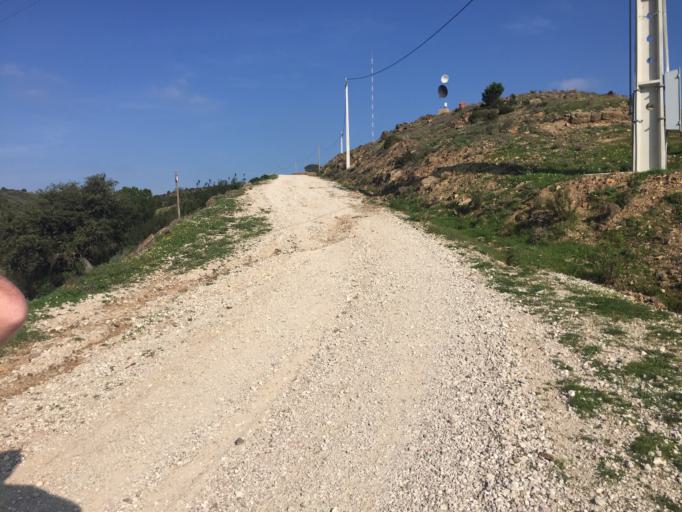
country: PT
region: Faro
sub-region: Castro Marim
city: Castro Marim
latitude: 37.2398
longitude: -7.5581
